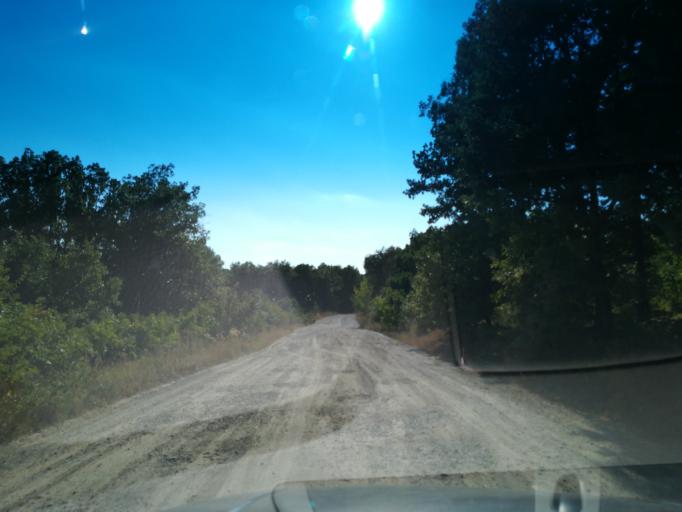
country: BG
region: Khaskovo
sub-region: Obshtina Mineralni Bani
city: Mineralni Bani
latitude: 41.9715
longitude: 25.3287
